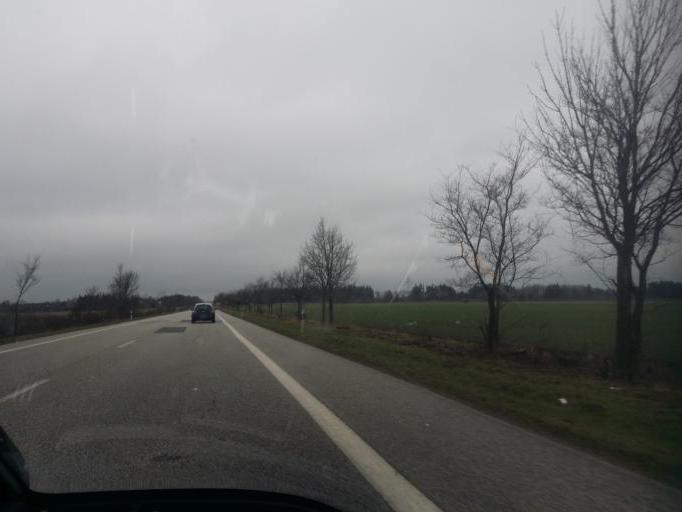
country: DE
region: Schleswig-Holstein
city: Bargum
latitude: 54.6949
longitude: 8.9571
